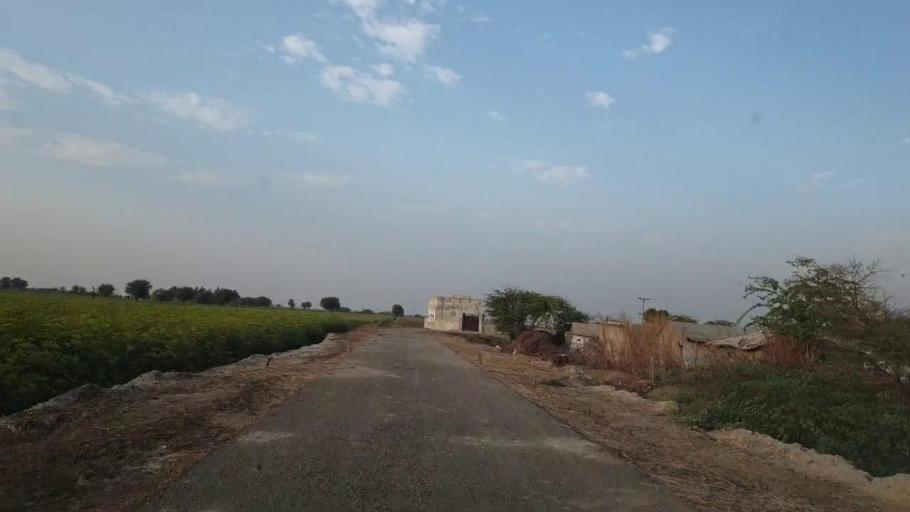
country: PK
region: Sindh
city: Pithoro
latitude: 25.5955
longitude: 69.3117
